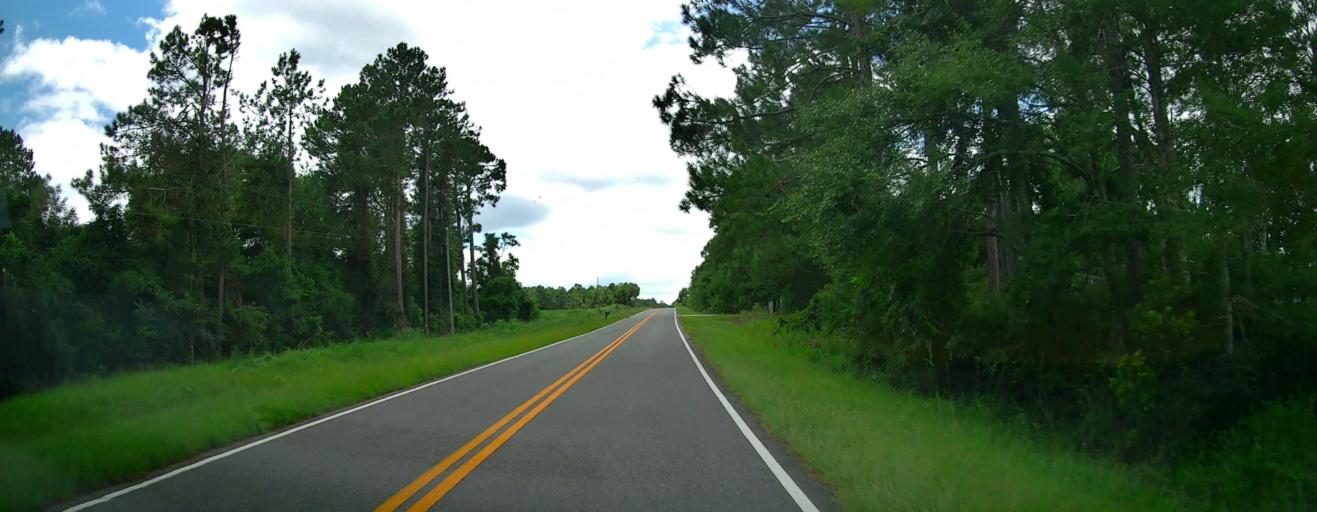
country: US
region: Georgia
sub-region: Turner County
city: Ashburn
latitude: 31.6913
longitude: -83.4762
